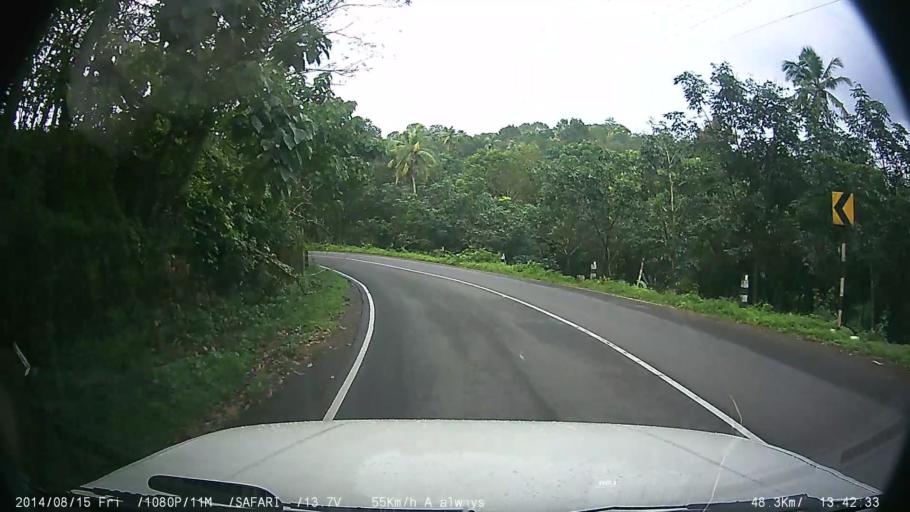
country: IN
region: Kerala
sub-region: Kottayam
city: Palackattumala
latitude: 9.7569
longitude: 76.5835
